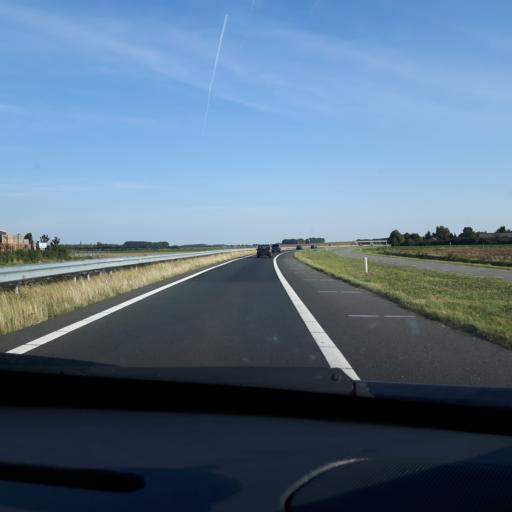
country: NL
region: Zeeland
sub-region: Gemeente Vlissingen
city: Vlissingen
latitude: 51.3393
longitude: 3.5695
